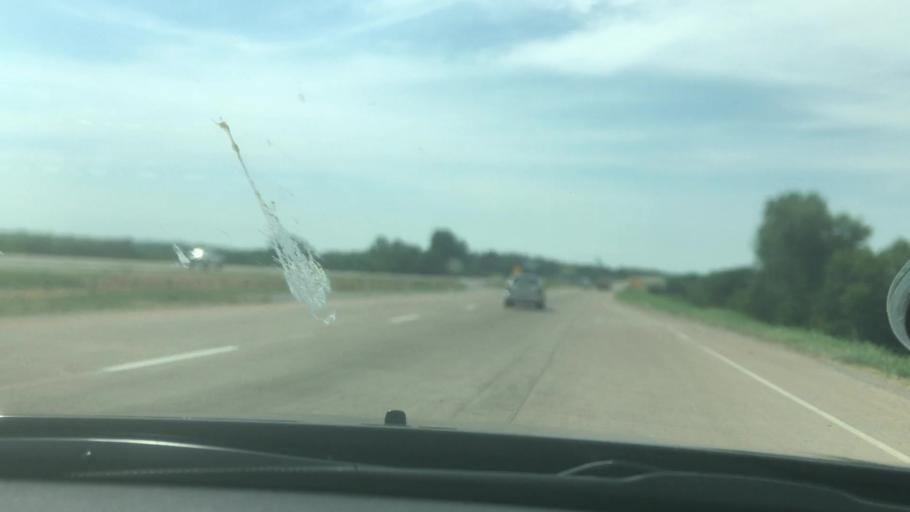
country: US
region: Oklahoma
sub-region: Garvin County
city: Pauls Valley
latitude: 34.7355
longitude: -97.2602
